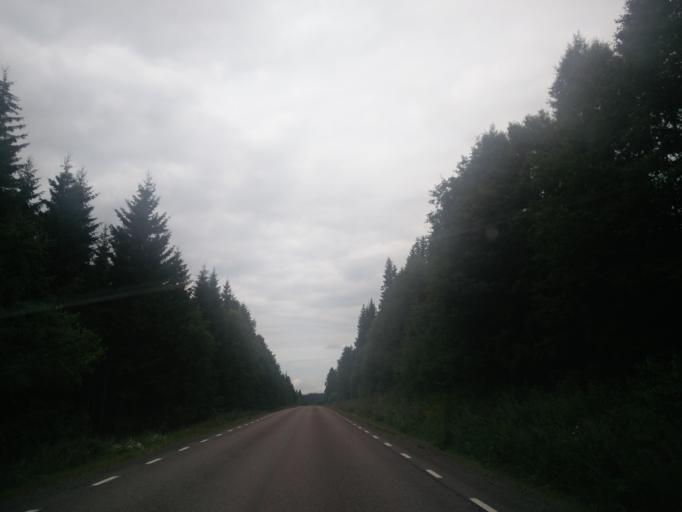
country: SE
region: Vaermland
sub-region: Torsby Kommun
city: Torsby
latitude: 59.9426
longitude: 12.7437
